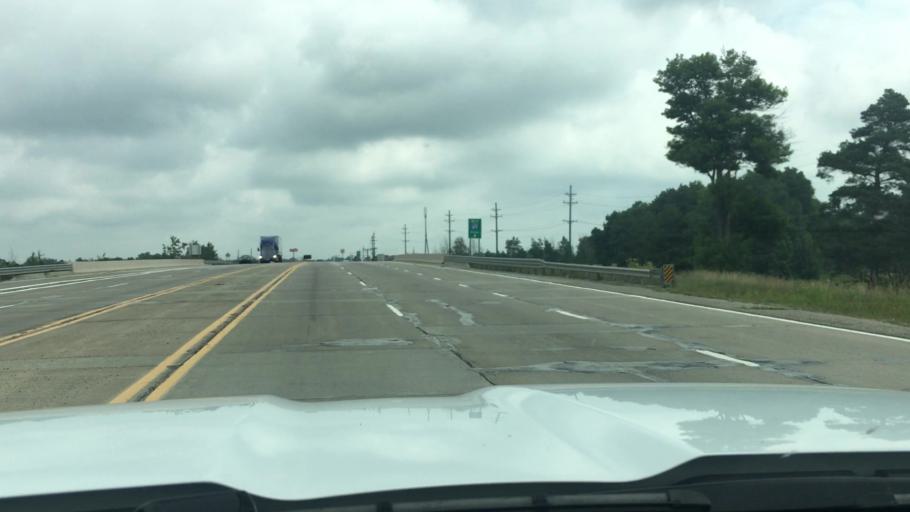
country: US
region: Michigan
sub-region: Lapeer County
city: Imlay City
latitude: 42.9998
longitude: -83.0711
